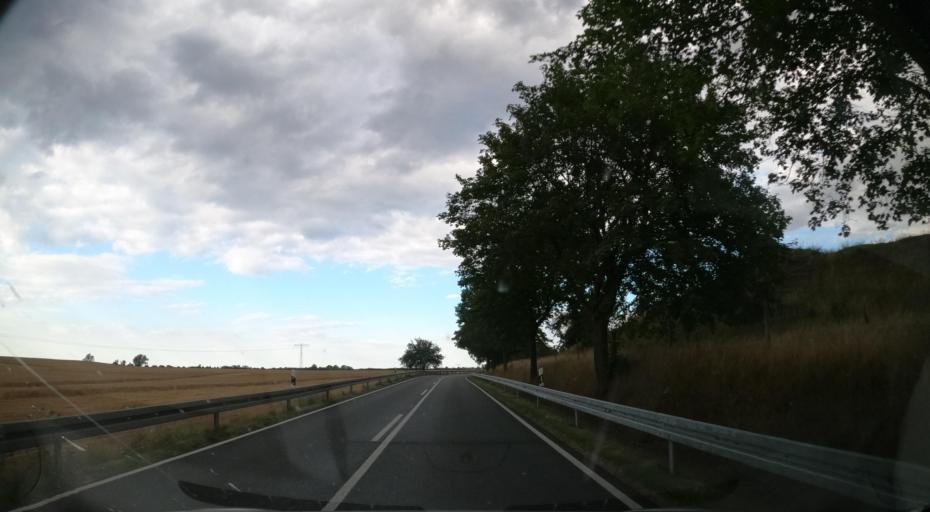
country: DE
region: Brandenburg
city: Goritz
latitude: 53.4955
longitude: 13.8939
